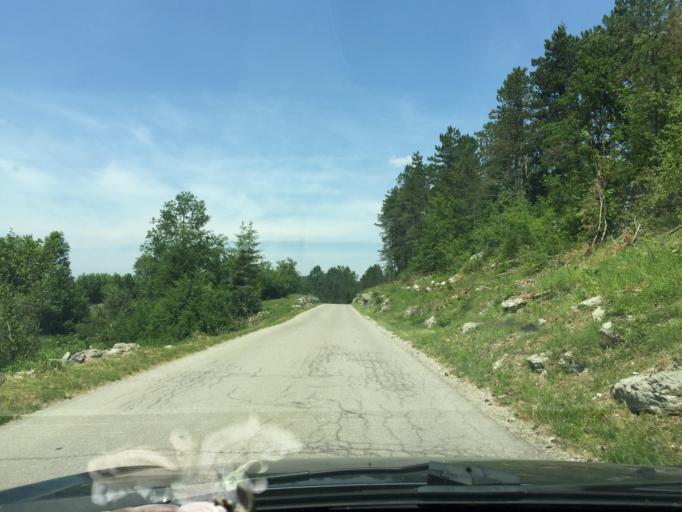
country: HR
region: Istarska
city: Buzet
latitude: 45.4554
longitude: 14.1447
